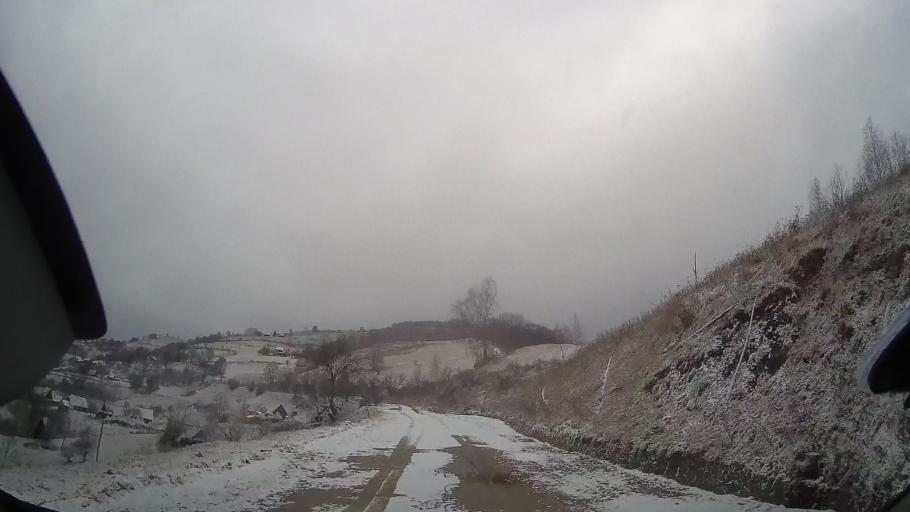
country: RO
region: Cluj
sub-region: Comuna Maguri-Racatau
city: Maguri-Racatau
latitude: 46.6605
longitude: 23.1919
